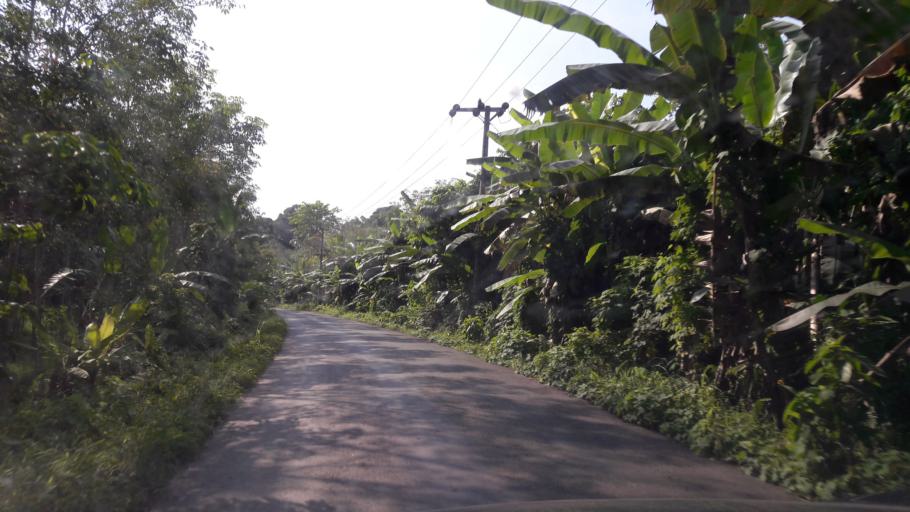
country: ID
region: South Sumatra
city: Prabumulih
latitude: -3.2896
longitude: 104.2201
